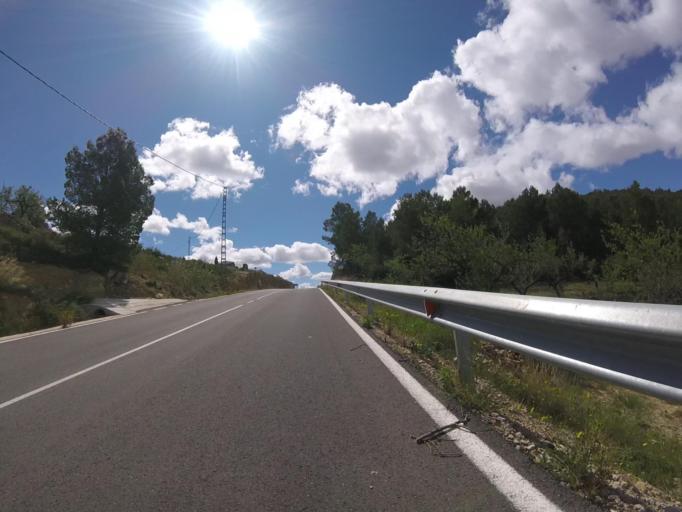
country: ES
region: Valencia
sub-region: Provincia de Castello
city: Culla
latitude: 40.2748
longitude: -0.1109
